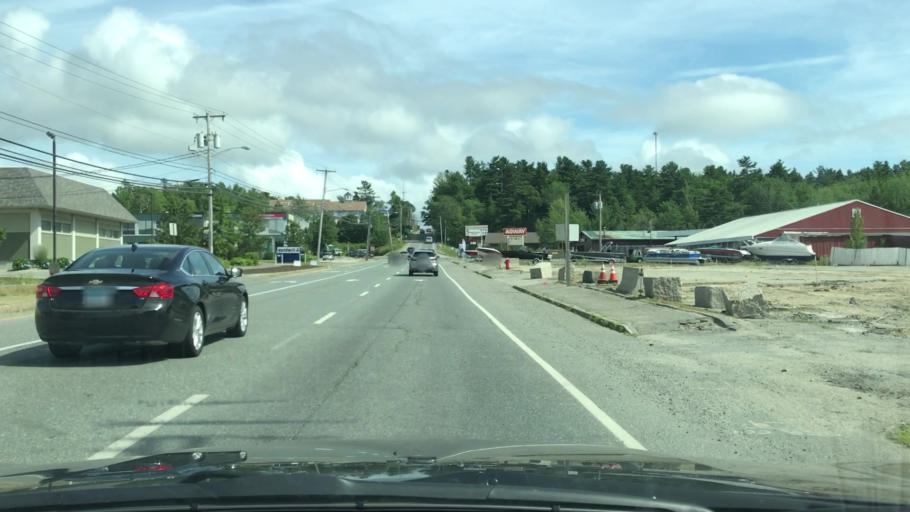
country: US
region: Maine
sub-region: Hancock County
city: Ellsworth
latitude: 44.5311
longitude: -68.4063
